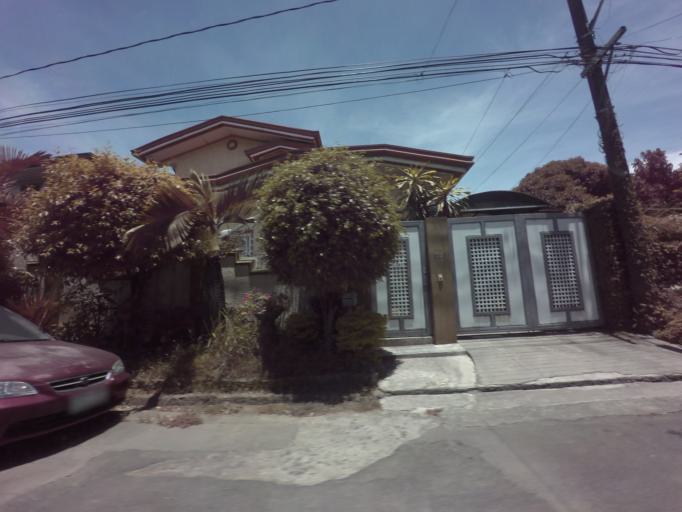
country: PH
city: Sambayanihan People's Village
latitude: 14.4874
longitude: 121.0359
